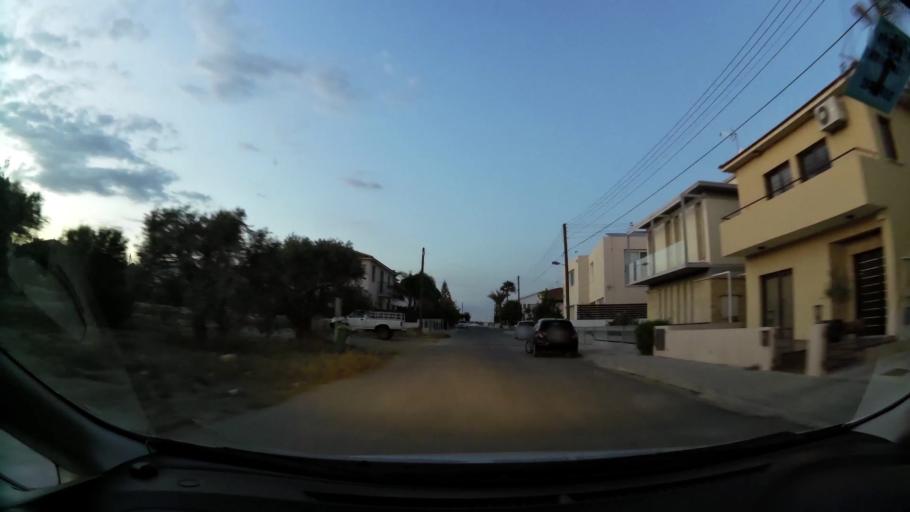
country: CY
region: Larnaka
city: Larnaca
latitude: 34.9115
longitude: 33.5900
